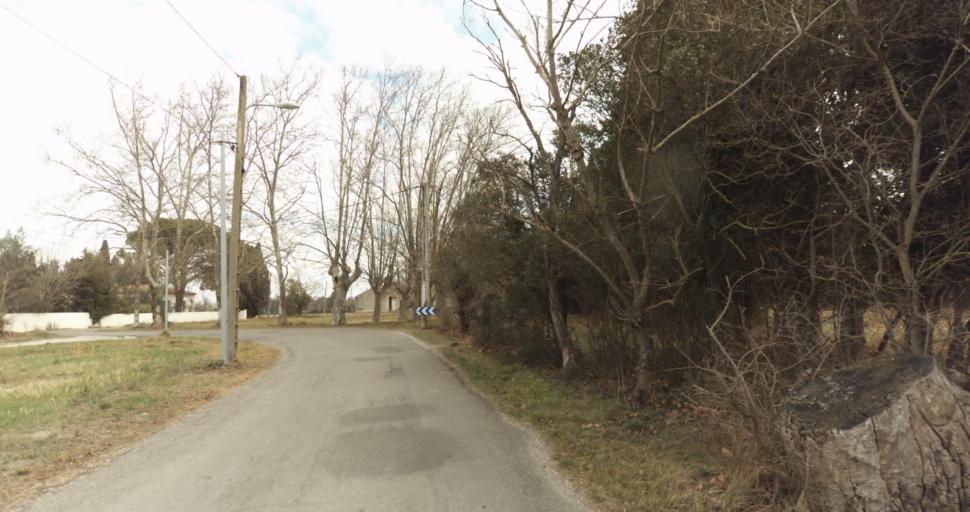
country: FR
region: Provence-Alpes-Cote d'Azur
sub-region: Departement du Vaucluse
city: Montfavet
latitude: 43.9376
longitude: 4.8548
